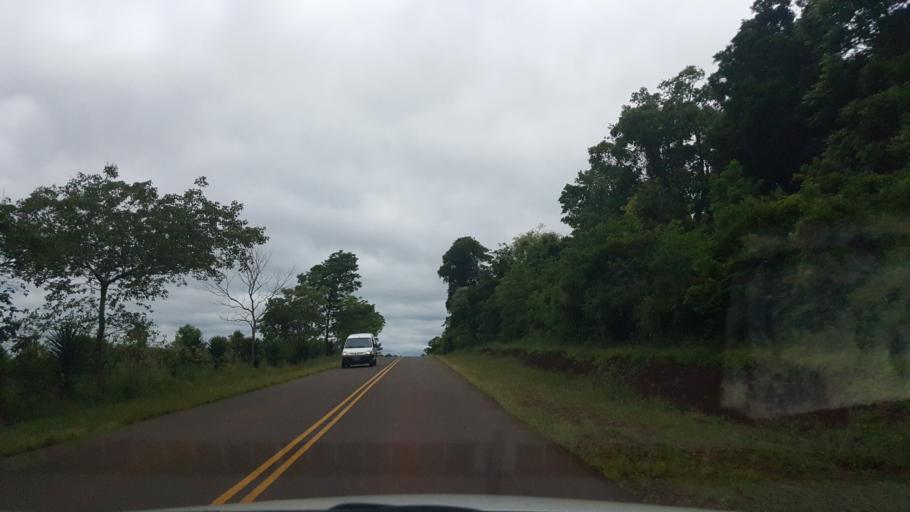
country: AR
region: Misiones
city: Capiovi
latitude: -26.9613
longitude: -55.0915
